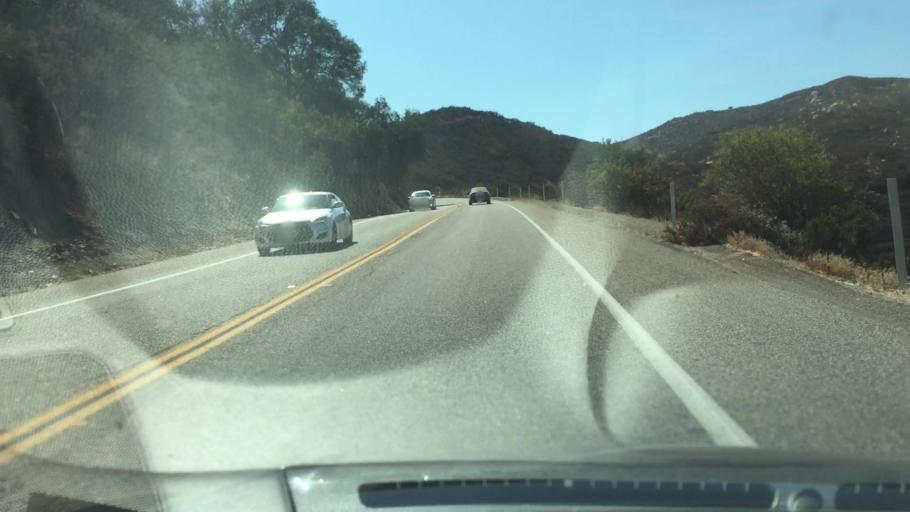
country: US
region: California
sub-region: San Diego County
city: Jamul
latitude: 32.7351
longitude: -116.8285
